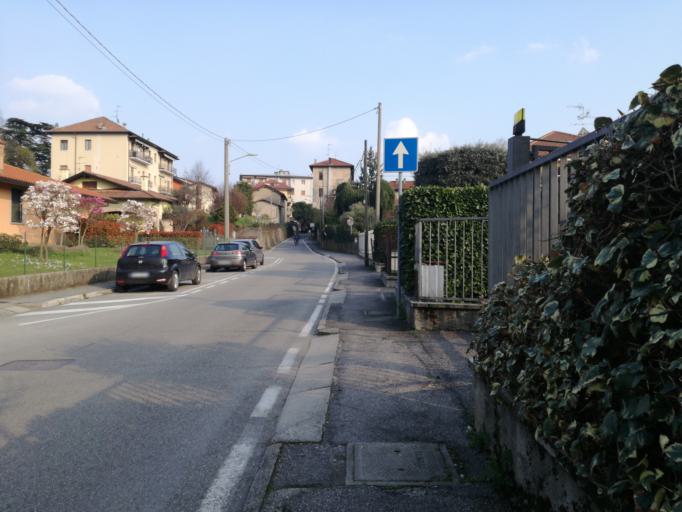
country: IT
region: Lombardy
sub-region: Provincia di Lecco
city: Verderio Inferiore
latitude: 45.6648
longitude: 9.4346
